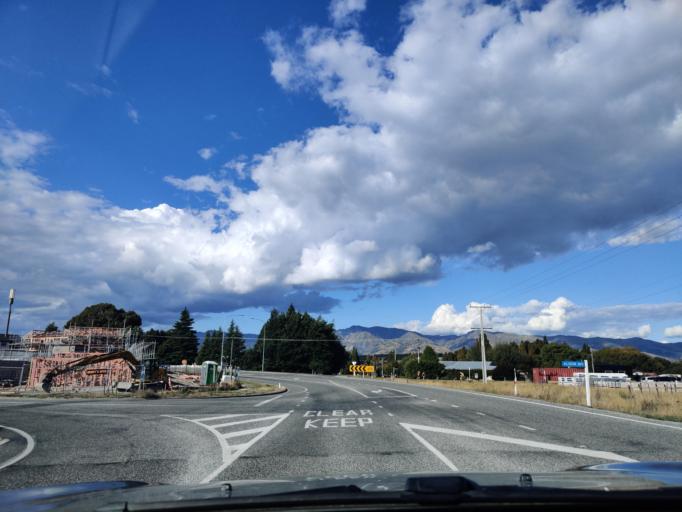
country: NZ
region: Otago
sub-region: Queenstown-Lakes District
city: Wanaka
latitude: -44.6839
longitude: 169.1886
